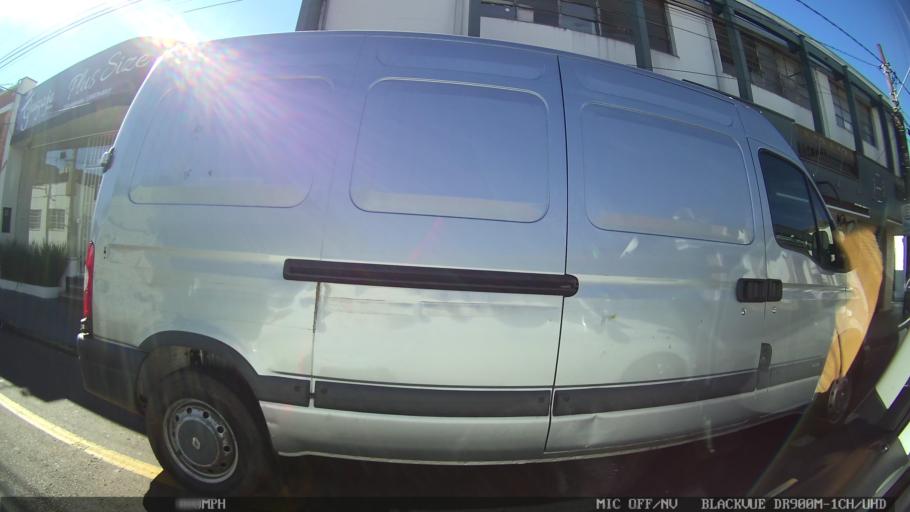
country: BR
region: Sao Paulo
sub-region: Franca
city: Franca
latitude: -20.5398
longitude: -47.3995
